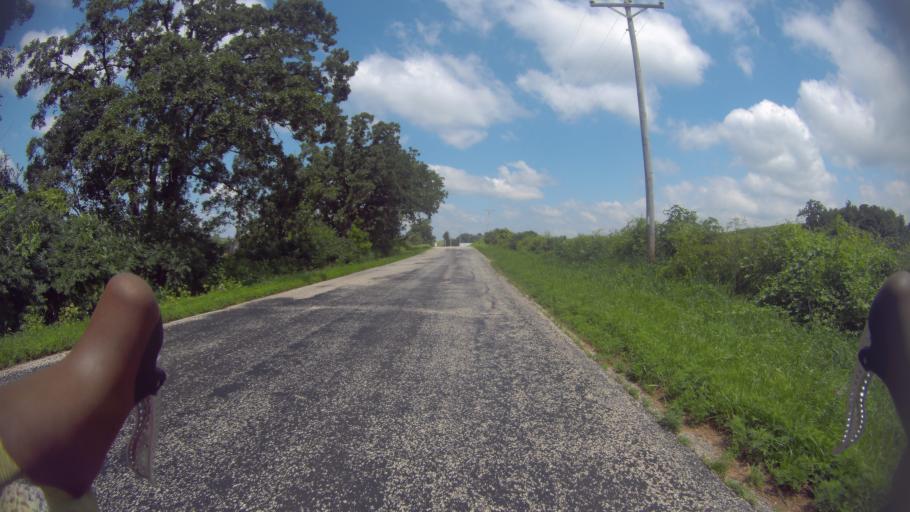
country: US
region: Wisconsin
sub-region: Columbia County
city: Lodi
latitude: 43.2358
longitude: -89.5998
